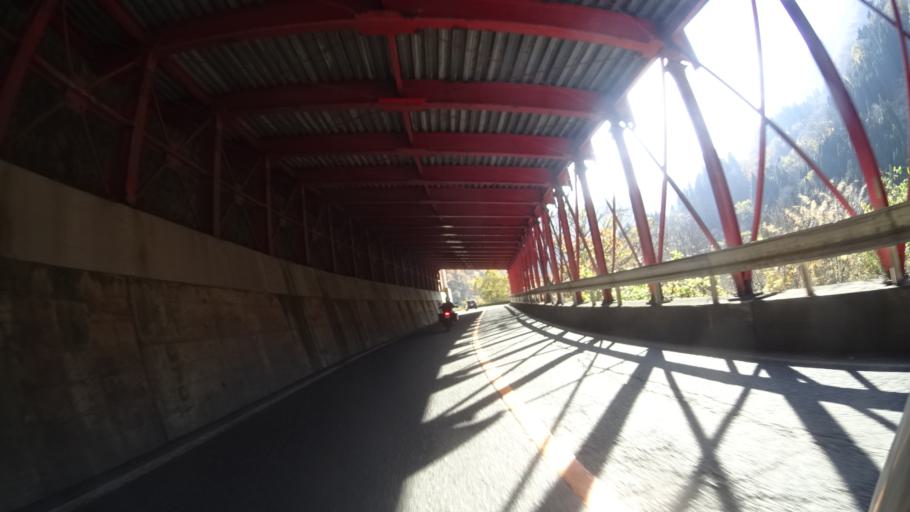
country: JP
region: Fukui
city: Ono
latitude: 35.9359
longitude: 136.6367
